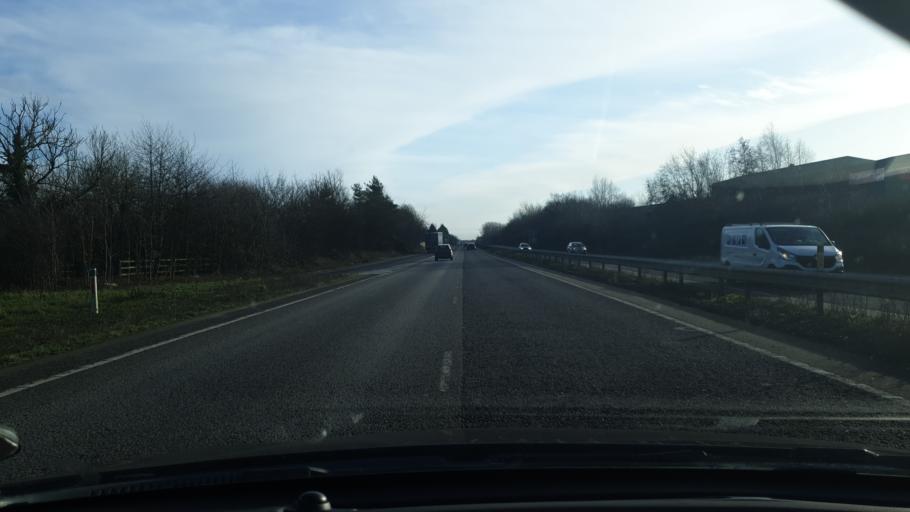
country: GB
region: England
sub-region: Suffolk
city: Woolpit
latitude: 52.2307
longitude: 0.8941
